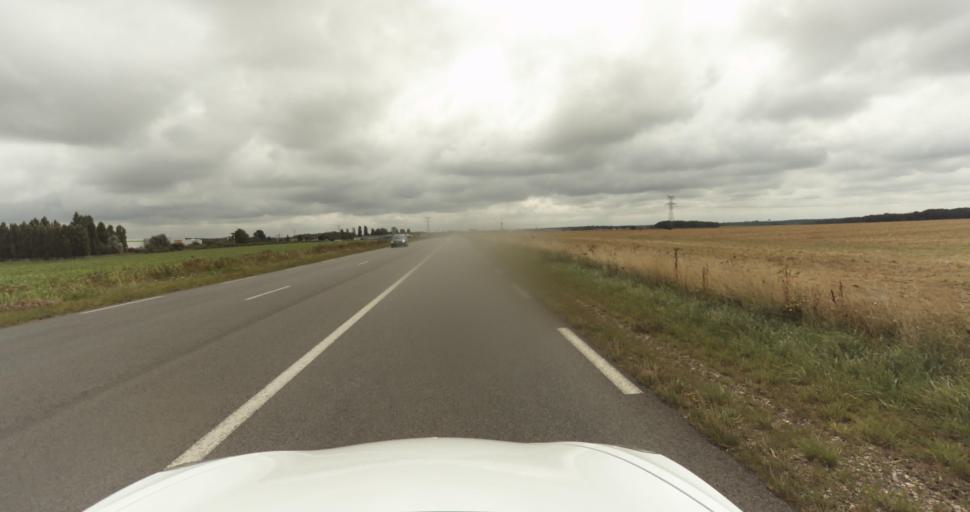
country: FR
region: Haute-Normandie
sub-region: Departement de l'Eure
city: Saint-Sebastien-de-Morsent
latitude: 49.0447
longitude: 1.0738
